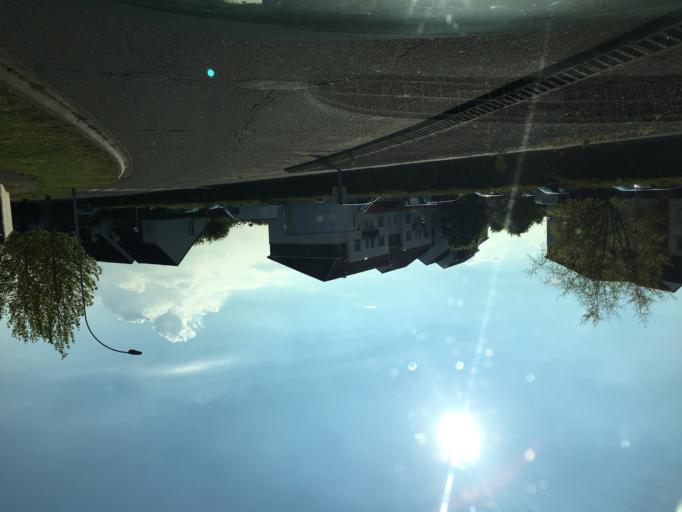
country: FR
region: Centre
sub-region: Departement du Loiret
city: Saran
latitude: 47.9337
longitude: 1.8908
